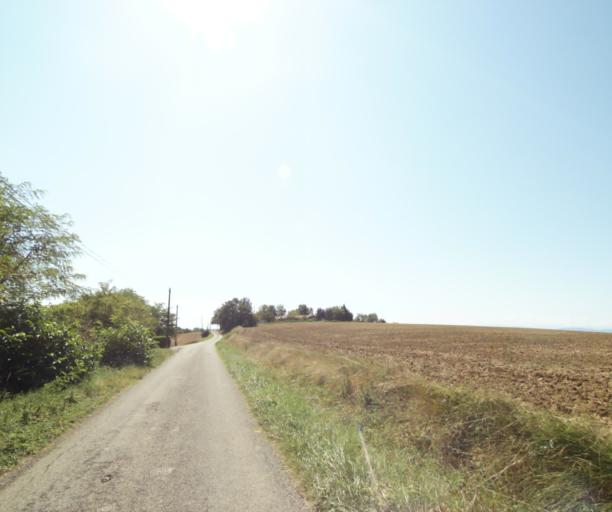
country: FR
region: Midi-Pyrenees
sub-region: Departement de l'Ariege
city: Lezat-sur-Leze
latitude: 43.2611
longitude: 1.3879
